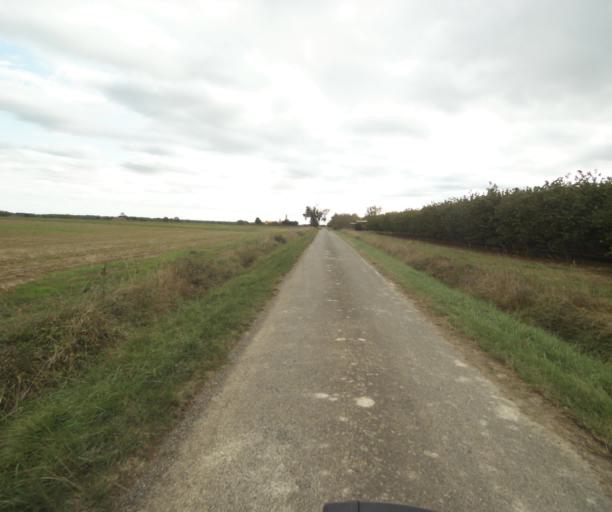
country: FR
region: Midi-Pyrenees
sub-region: Departement du Tarn-et-Garonne
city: Verdun-sur-Garonne
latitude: 43.8655
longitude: 1.1624
